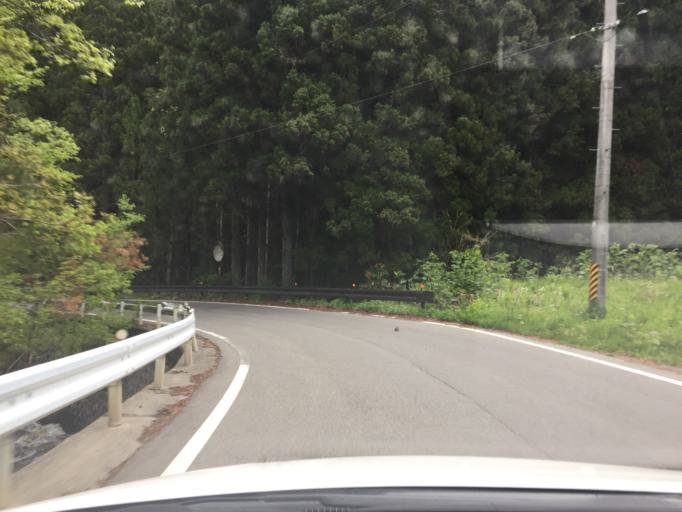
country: JP
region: Fukushima
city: Hobaramachi
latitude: 37.7254
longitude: 140.6416
